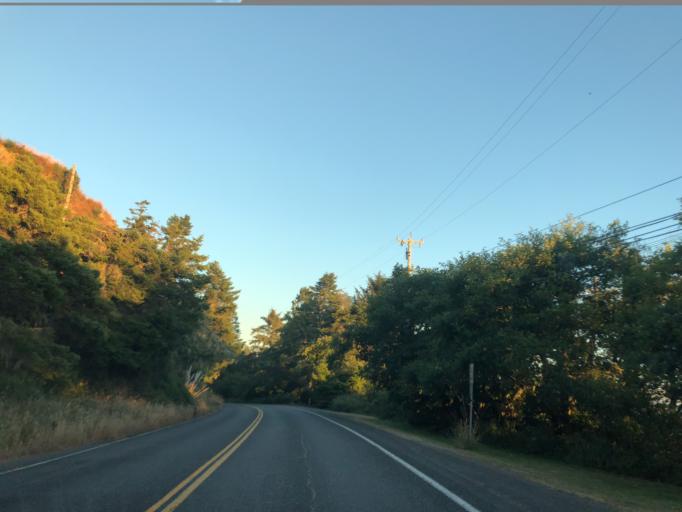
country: US
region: California
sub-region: Humboldt County
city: Westhaven-Moonstone
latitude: 41.0958
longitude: -124.1570
